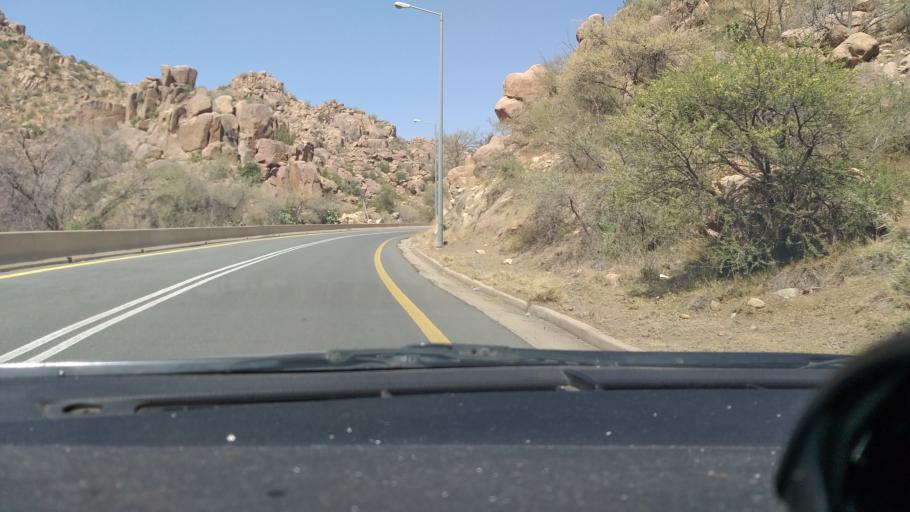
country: SA
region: Makkah
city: Ash Shafa
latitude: 21.0922
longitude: 40.3747
